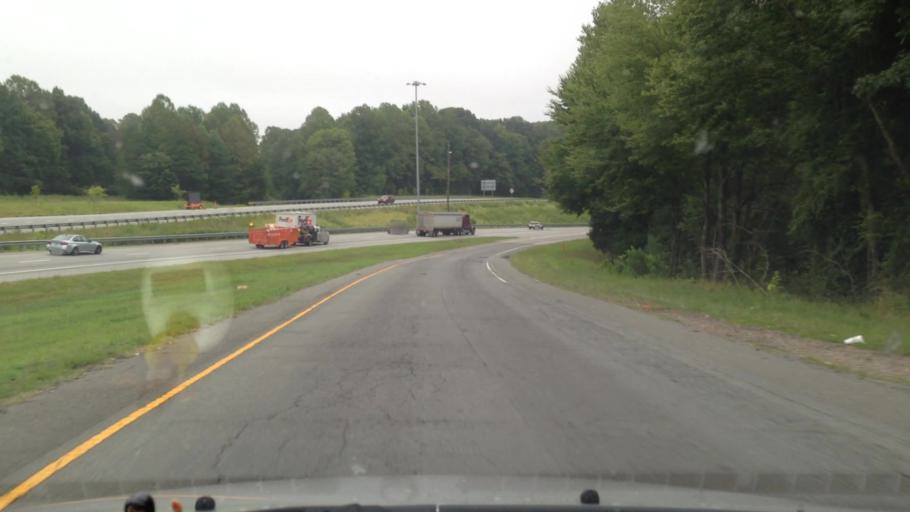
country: US
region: North Carolina
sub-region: Forsyth County
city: Kernersville
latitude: 36.1124
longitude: -80.0621
